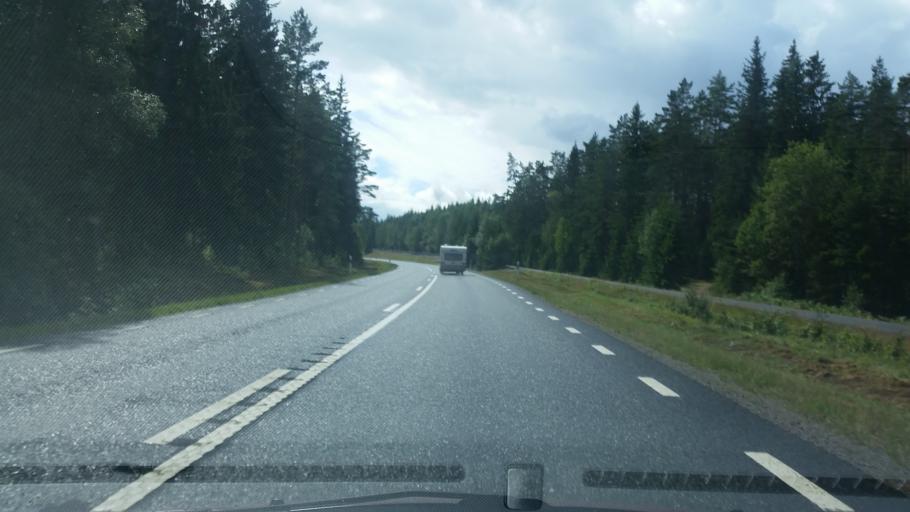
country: SE
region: Joenkoeping
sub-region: Gislaveds Kommun
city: Gislaved
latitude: 57.3798
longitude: 13.5789
